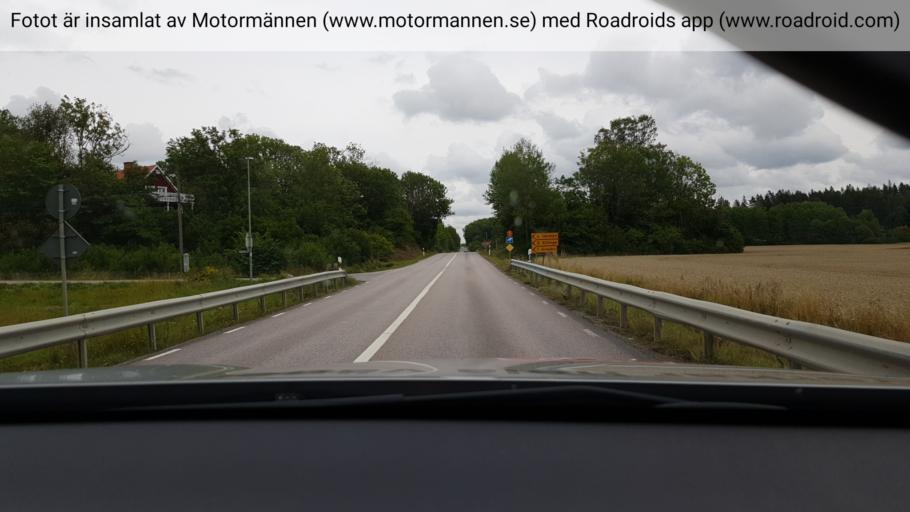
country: SE
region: Stockholm
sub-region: Sigtuna Kommun
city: Sigtuna
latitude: 59.6486
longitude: 17.6403
